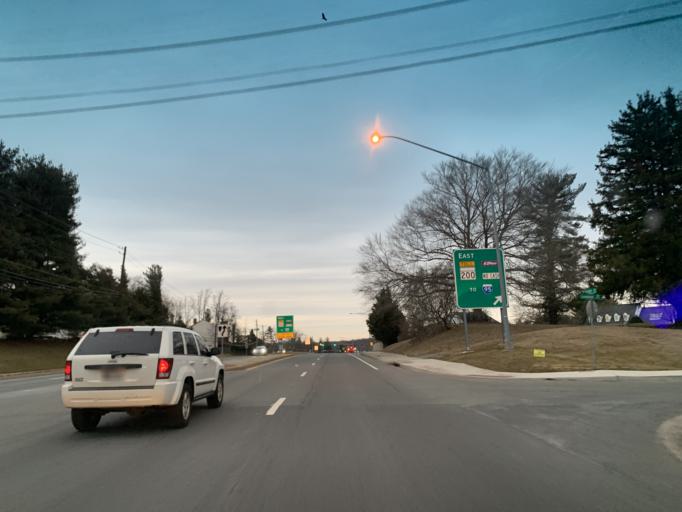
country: US
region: Maryland
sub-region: Montgomery County
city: Layhill
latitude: 39.0970
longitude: -77.0437
